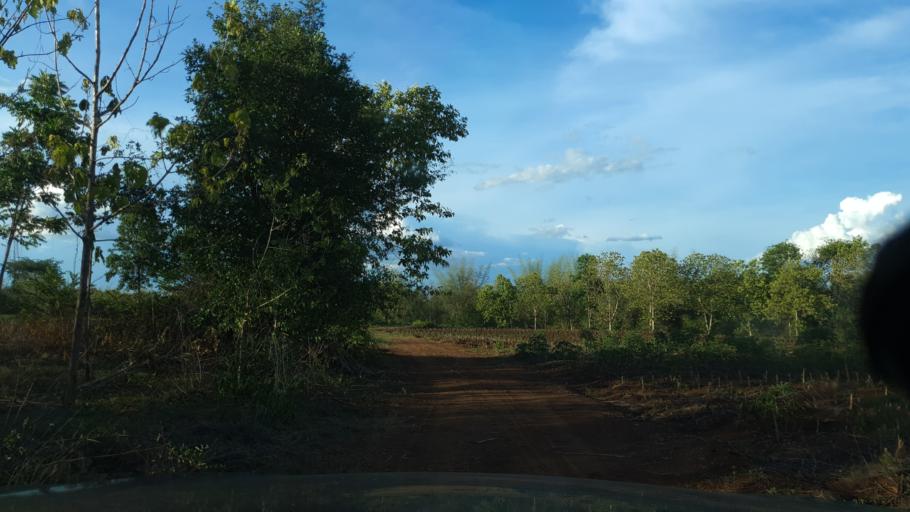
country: TH
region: Lampang
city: Sop Prap
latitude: 17.9605
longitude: 99.3517
